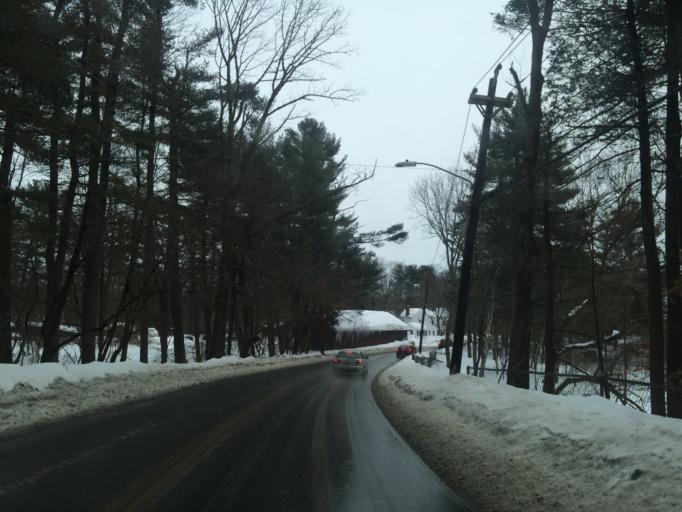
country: US
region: Massachusetts
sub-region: Middlesex County
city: Lincoln
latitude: 42.4087
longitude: -71.3263
